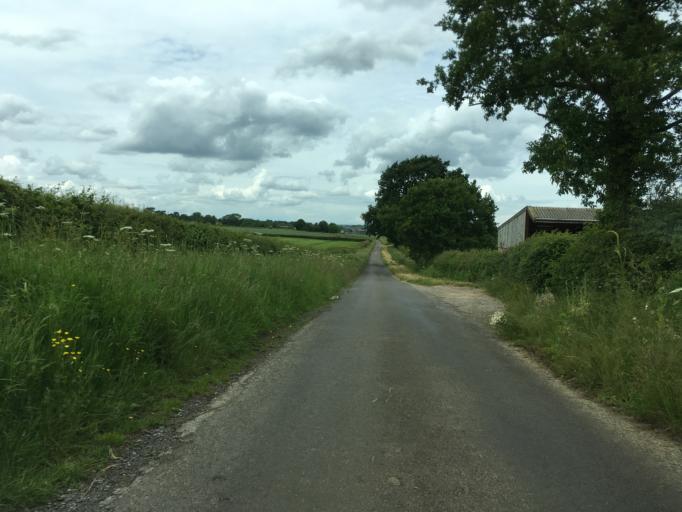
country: GB
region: England
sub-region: Wiltshire
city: Malmesbury
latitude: 51.5212
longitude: -2.1065
